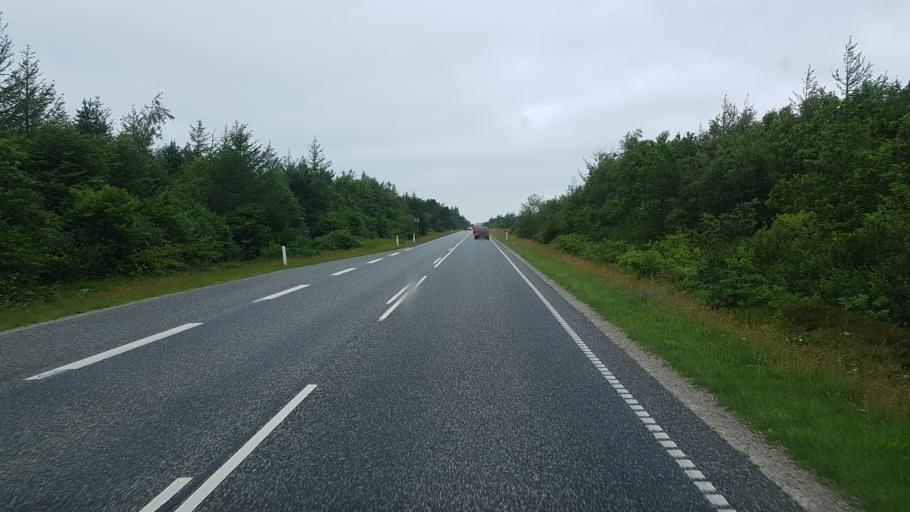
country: DK
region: Central Jutland
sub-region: Lemvig Kommune
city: Lemvig
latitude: 56.4500
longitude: 8.3495
